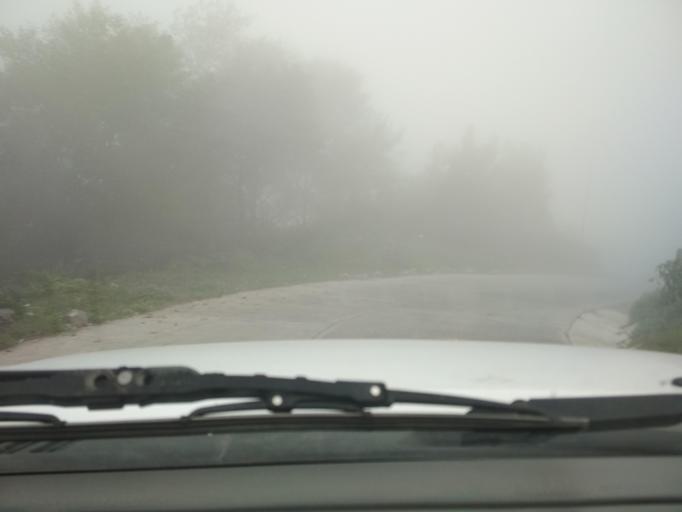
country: MX
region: Veracruz
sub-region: La Perla
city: Barrio de San Miguel
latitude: 18.9435
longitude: -97.1198
